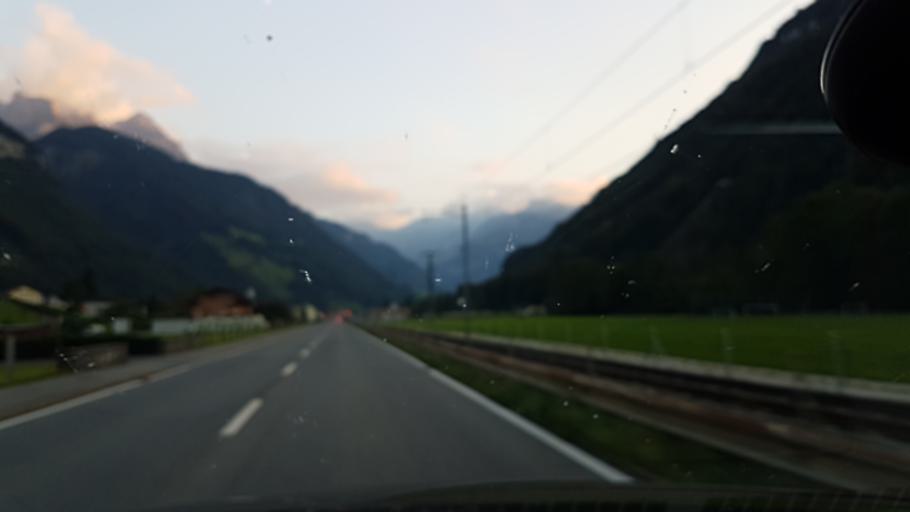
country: CH
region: Nidwalden
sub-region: Nidwalden
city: Dallenwil
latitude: 46.9164
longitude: 8.3965
